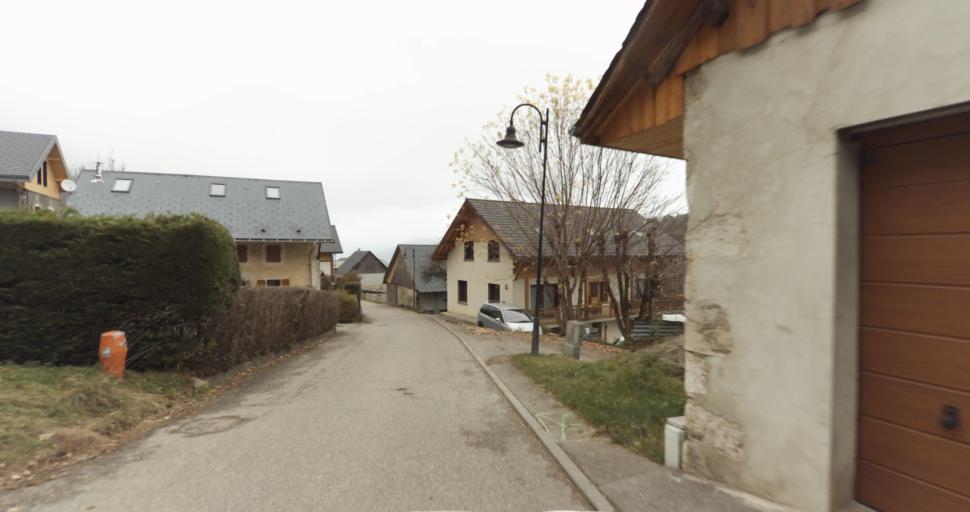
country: FR
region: Rhone-Alpes
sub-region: Departement de la Haute-Savoie
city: Doussard
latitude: 45.7977
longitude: 6.1893
